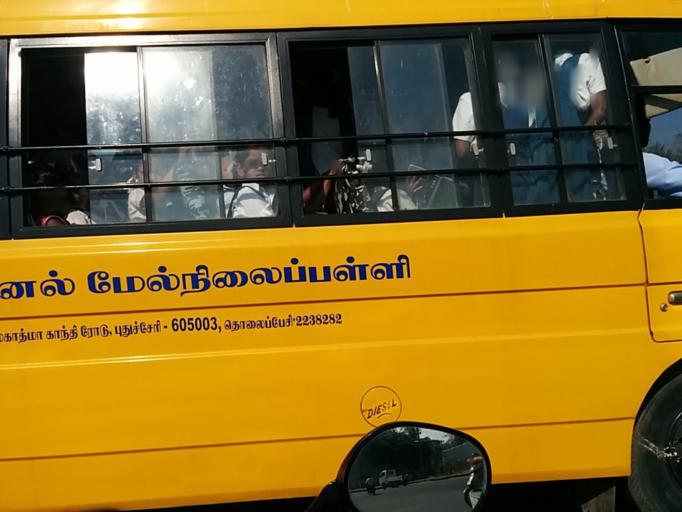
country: IN
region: Pondicherry
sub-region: Puducherry
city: Puducherry
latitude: 11.9564
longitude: 79.8266
